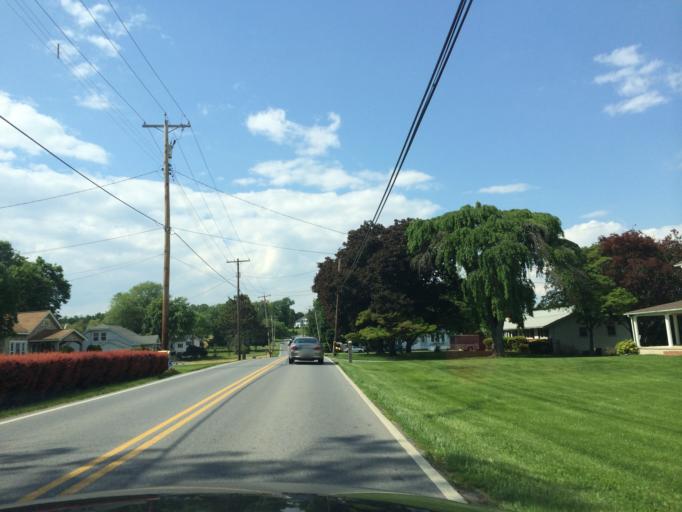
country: US
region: Maryland
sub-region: Carroll County
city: Sykesville
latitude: 39.3753
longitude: -77.0572
